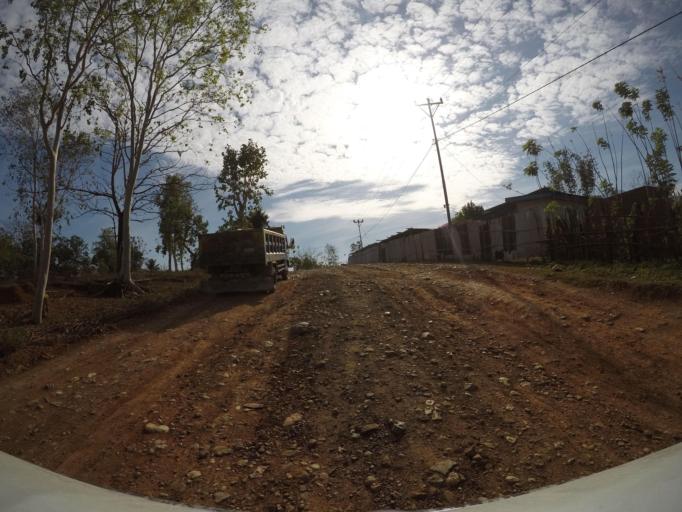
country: TL
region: Bobonaro
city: Maliana
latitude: -8.9281
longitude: 125.2034
